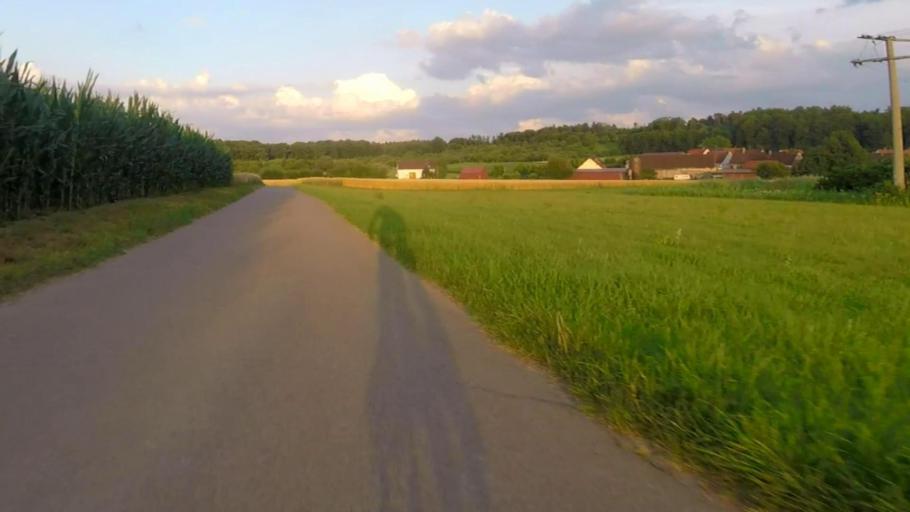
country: DE
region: Baden-Wuerttemberg
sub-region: Regierungsbezirk Stuttgart
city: Aspach
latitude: 48.9863
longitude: 9.3748
